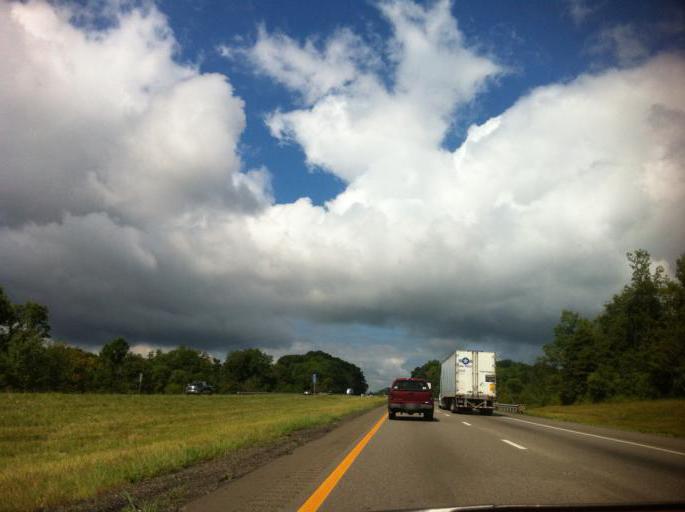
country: US
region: Ohio
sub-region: Trumbull County
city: Churchill
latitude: 41.1589
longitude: -80.6289
